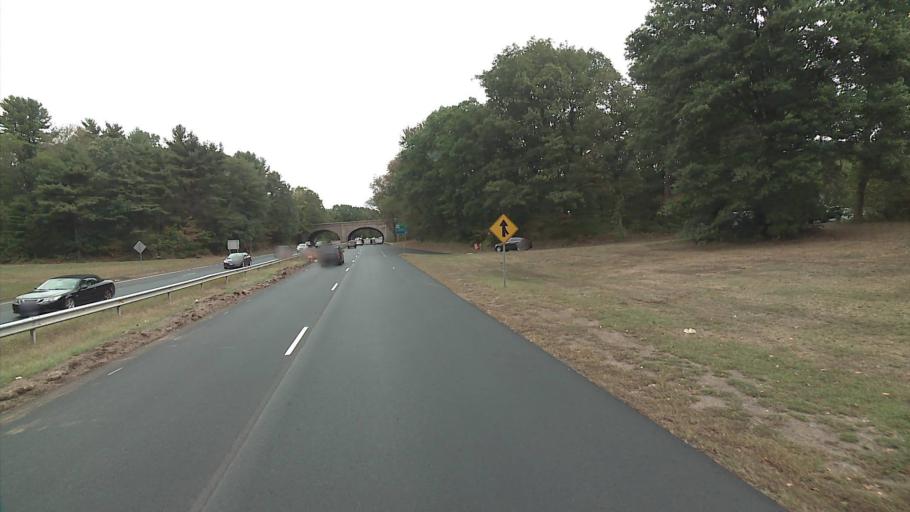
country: US
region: Connecticut
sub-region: New Haven County
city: Orange
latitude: 41.3047
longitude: -73.0340
